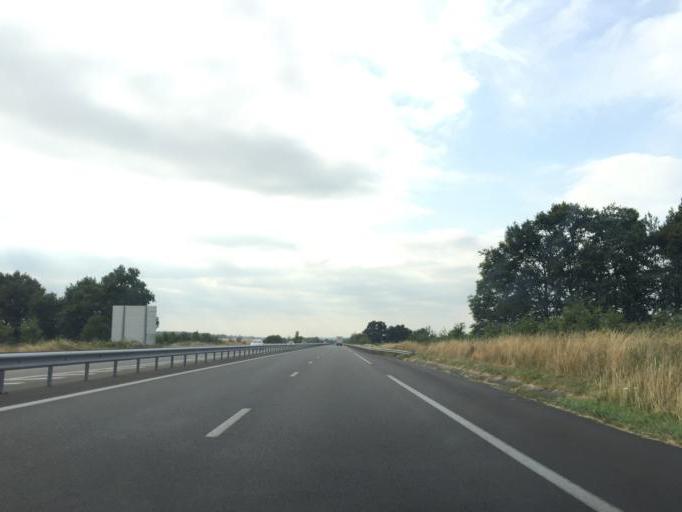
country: FR
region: Auvergne
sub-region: Departement de l'Allier
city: Saint-Francois
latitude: 46.4594
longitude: 3.8928
